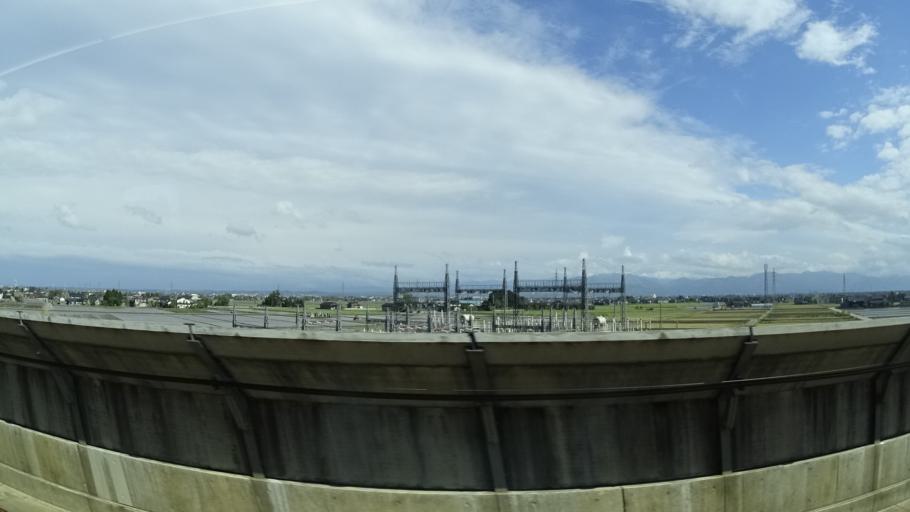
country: JP
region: Toyama
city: Takaoka
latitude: 36.7068
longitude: 136.9505
